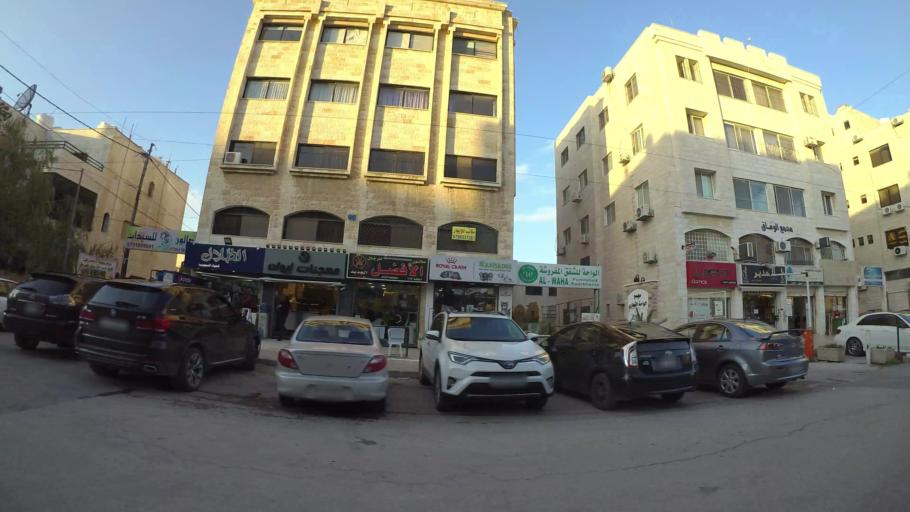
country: JO
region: Amman
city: Al Jubayhah
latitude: 31.9928
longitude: 35.8715
